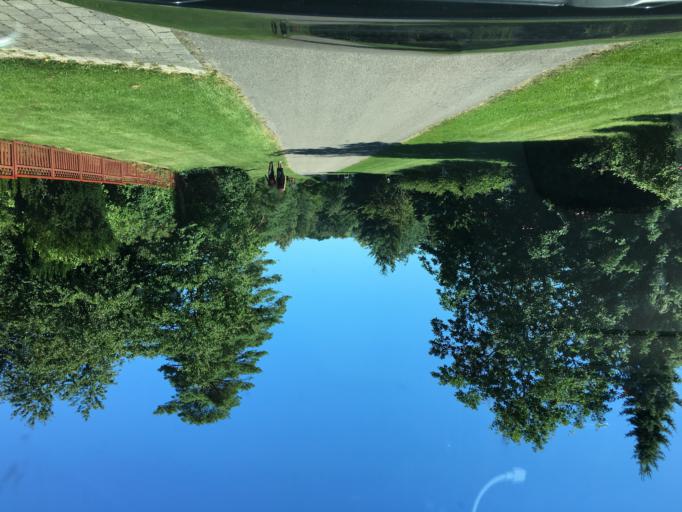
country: DK
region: Capital Region
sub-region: Gribskov Kommune
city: Helsinge
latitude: 56.0928
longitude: 12.1650
